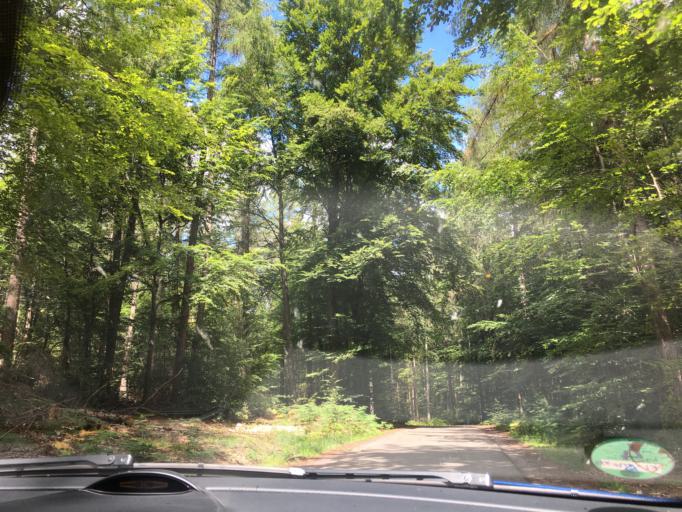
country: DE
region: Rheinland-Pfalz
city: Leimen
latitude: 49.2800
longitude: 7.8242
